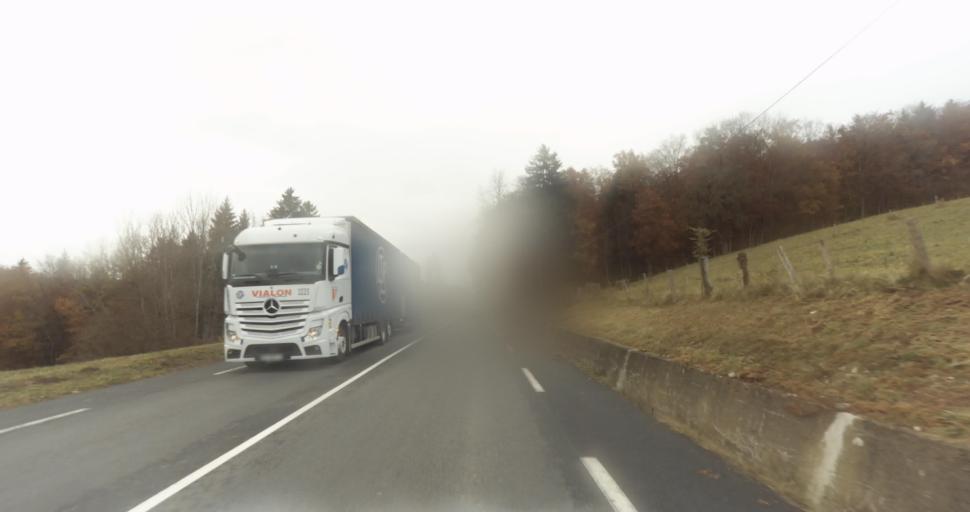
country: FR
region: Rhone-Alpes
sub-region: Departement de la Haute-Savoie
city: Evires
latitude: 46.0114
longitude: 6.2085
